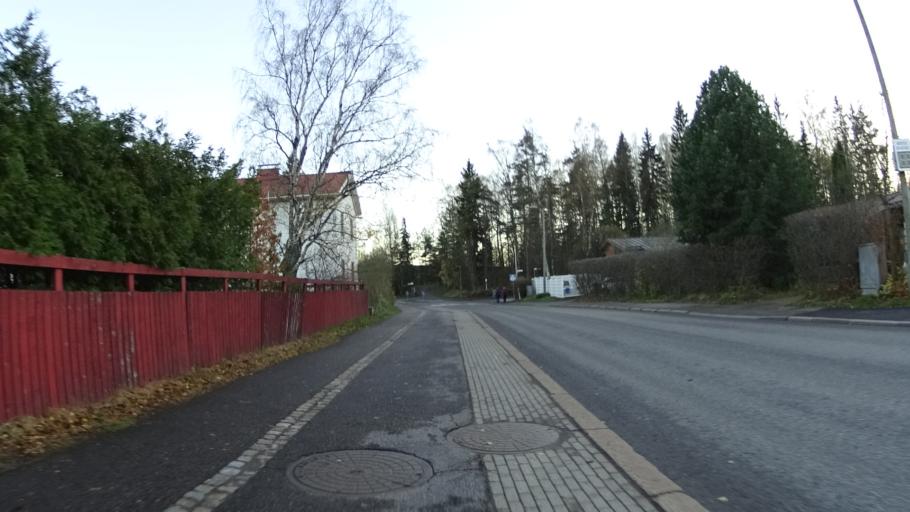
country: FI
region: Uusimaa
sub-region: Helsinki
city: Helsinki
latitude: 60.2451
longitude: 24.9436
